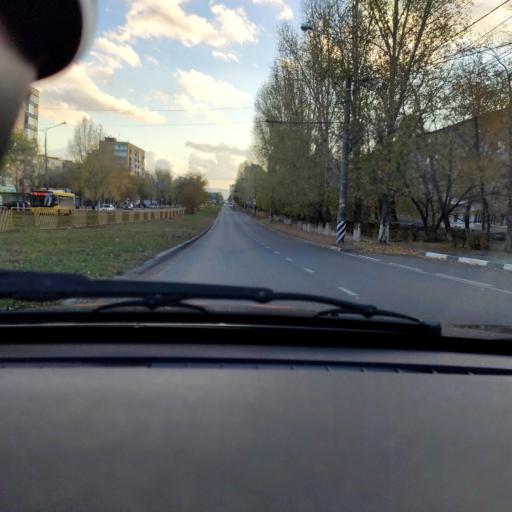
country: RU
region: Samara
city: Zhigulevsk
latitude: 53.4856
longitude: 49.4740
